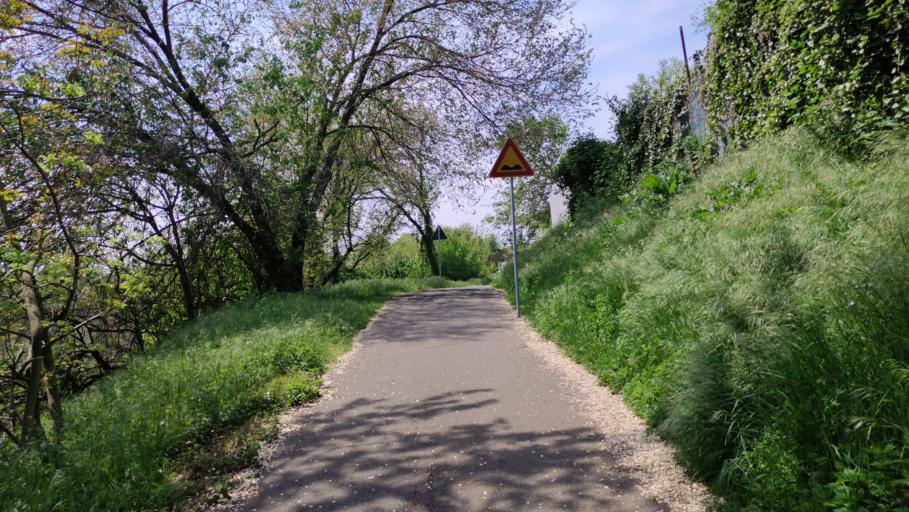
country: IT
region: Piedmont
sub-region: Provincia di Torino
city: Nichelino
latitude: 45.0080
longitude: 7.6532
